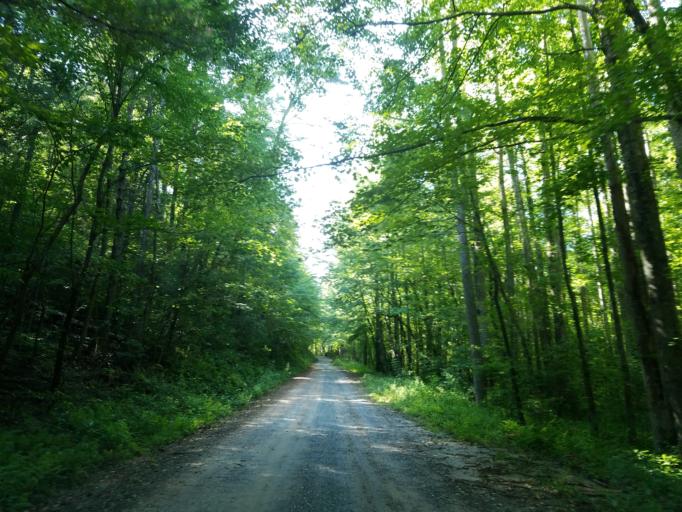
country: US
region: Georgia
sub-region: Dawson County
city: Dawsonville
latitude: 34.5859
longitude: -84.1884
